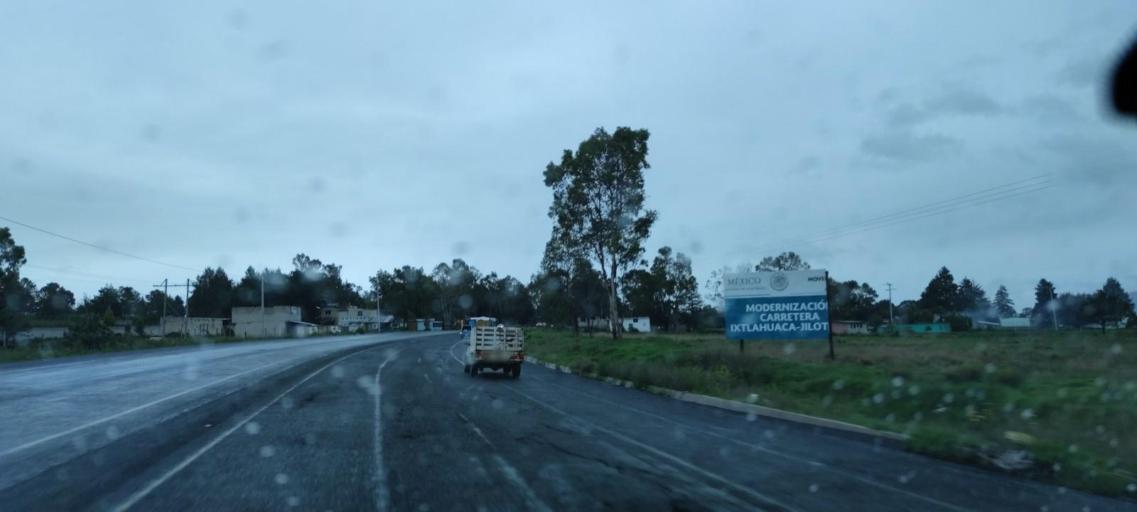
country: MX
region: Mexico
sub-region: Jilotepec
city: Doxhicho
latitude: 19.9094
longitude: -99.6104
